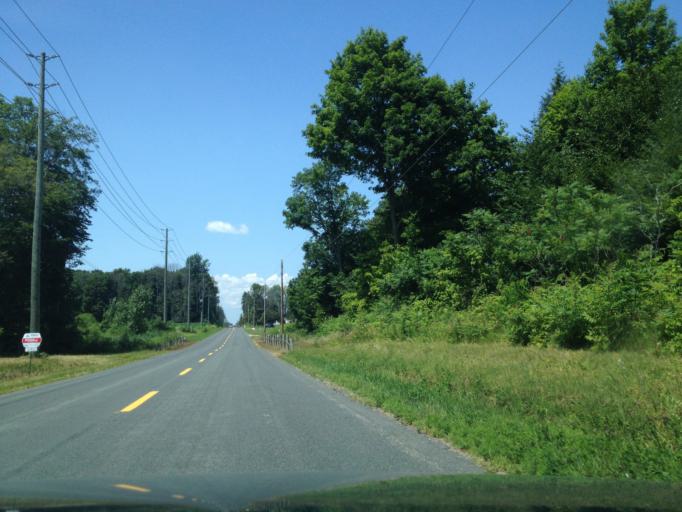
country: CA
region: Ontario
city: Aylmer
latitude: 42.6443
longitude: -80.7440
